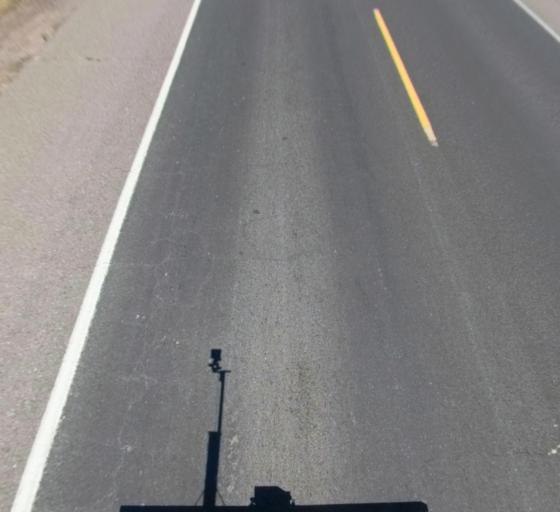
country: US
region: California
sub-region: Madera County
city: Parkwood
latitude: 36.9238
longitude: -120.0621
